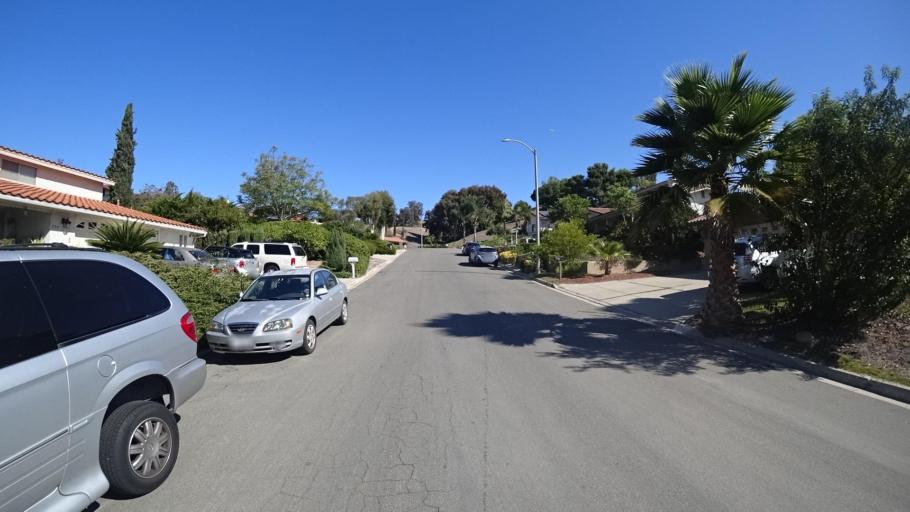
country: US
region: California
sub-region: San Diego County
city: Bonita
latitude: 32.6675
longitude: -117.0055
